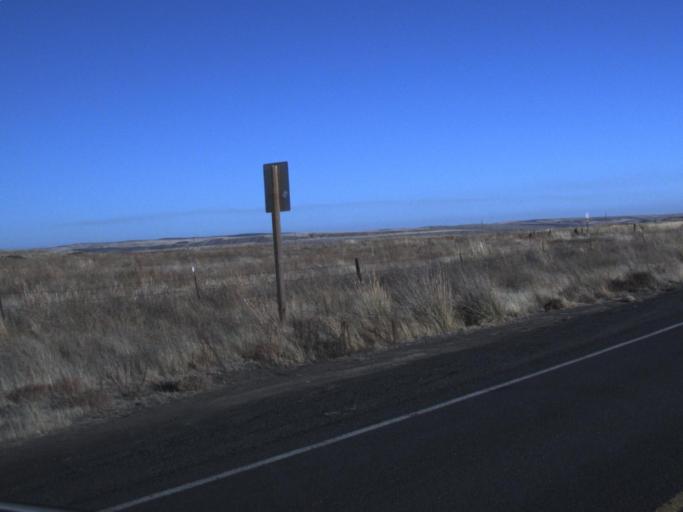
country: US
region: Washington
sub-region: Walla Walla County
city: Waitsburg
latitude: 46.6570
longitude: -118.2659
